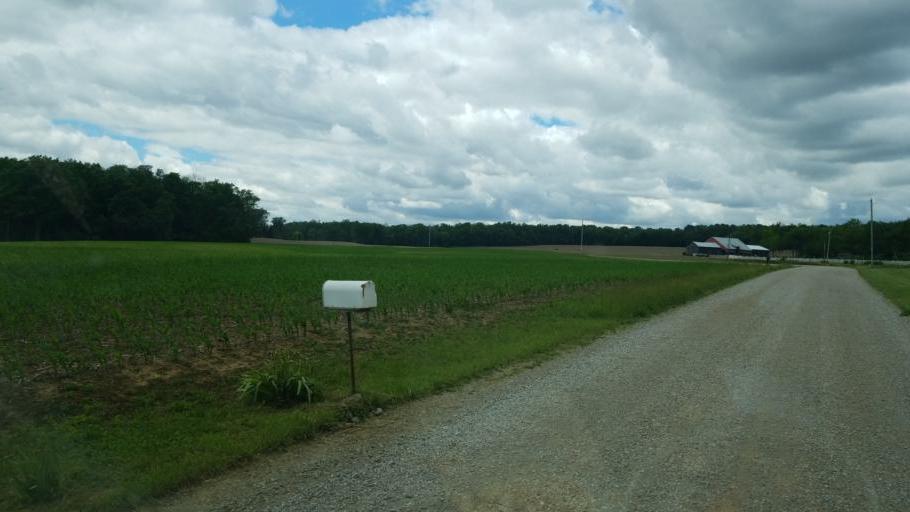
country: US
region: Ohio
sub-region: Richland County
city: Lexington
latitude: 40.6362
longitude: -82.6549
